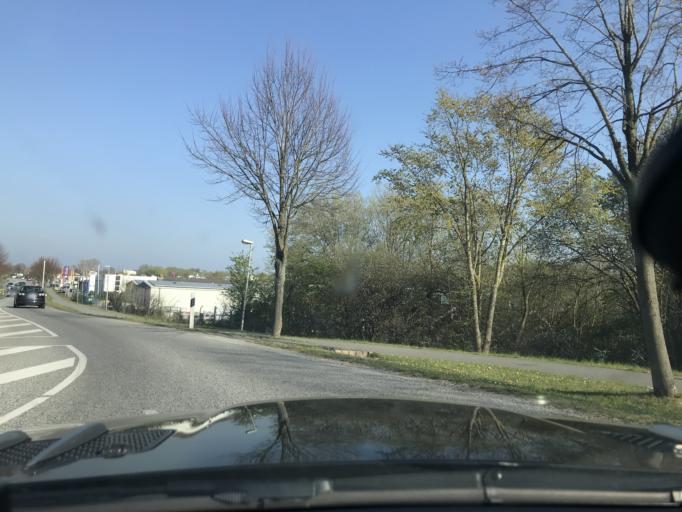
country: DE
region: Schleswig-Holstein
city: Heiligenhafen
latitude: 54.3652
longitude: 11.0041
